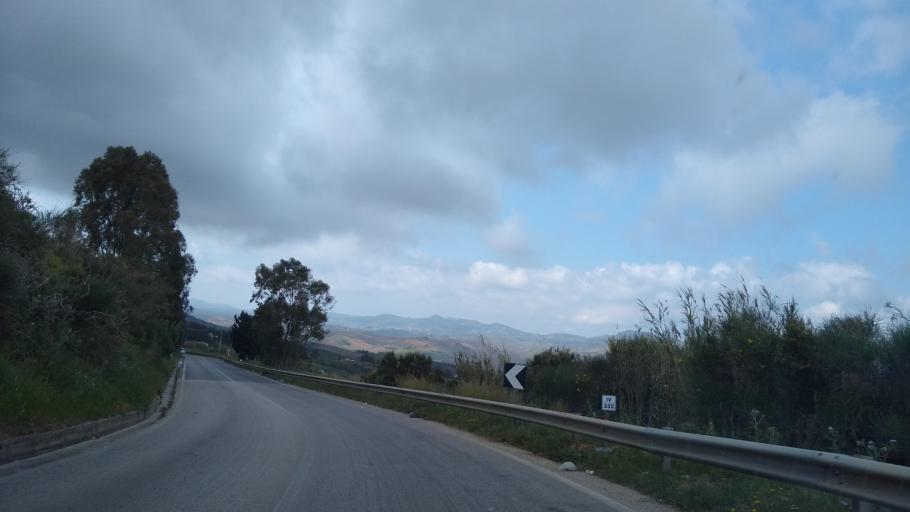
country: IT
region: Sicily
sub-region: Trapani
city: Alcamo
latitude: 37.9784
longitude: 12.9361
